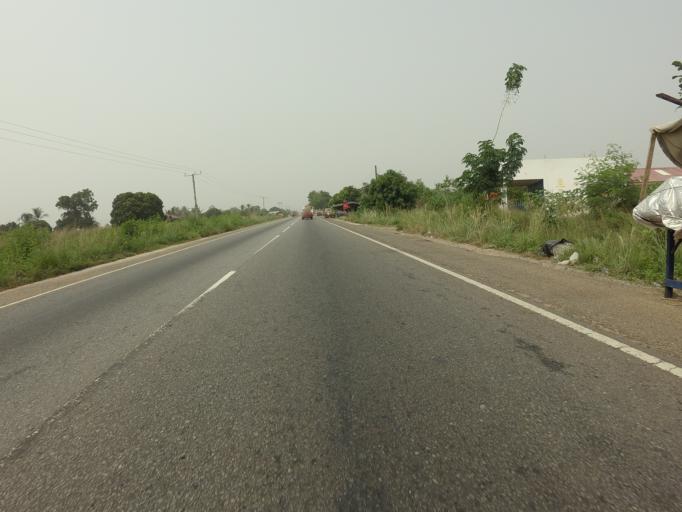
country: GH
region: Volta
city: Anloga
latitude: 5.8935
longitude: 0.4974
